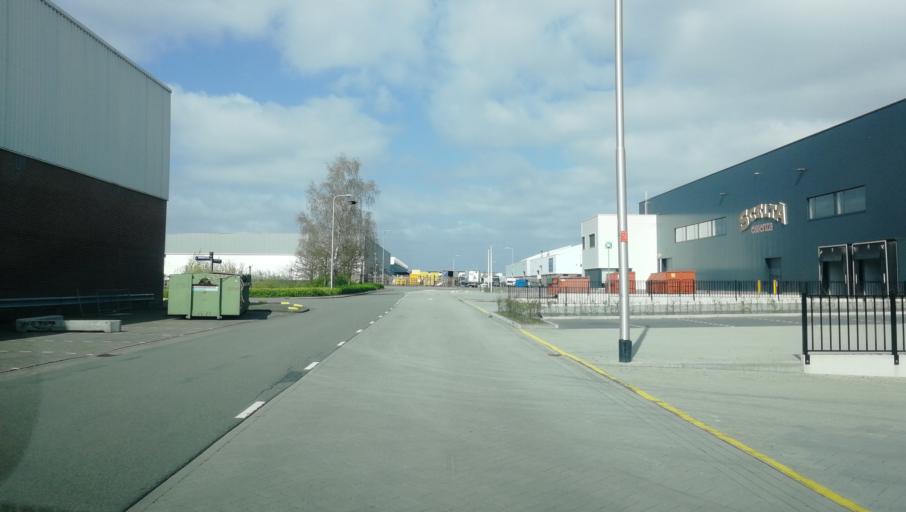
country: NL
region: Limburg
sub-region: Gemeente Venlo
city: Venlo
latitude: 51.4050
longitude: 6.1342
